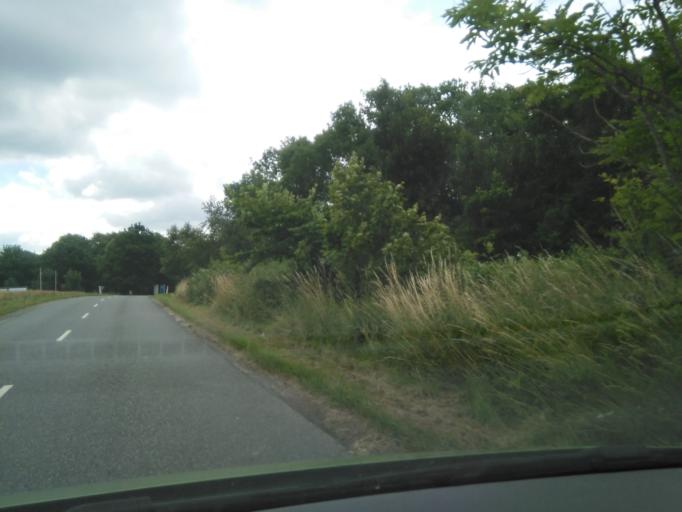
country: DK
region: Central Jutland
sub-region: Arhus Kommune
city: Logten
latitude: 56.2464
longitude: 10.3334
